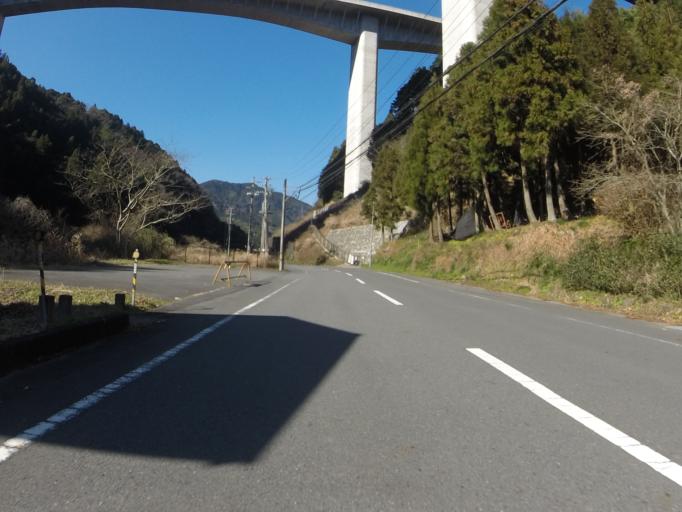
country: JP
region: Shizuoka
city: Fujinomiya
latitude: 35.1133
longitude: 138.4878
